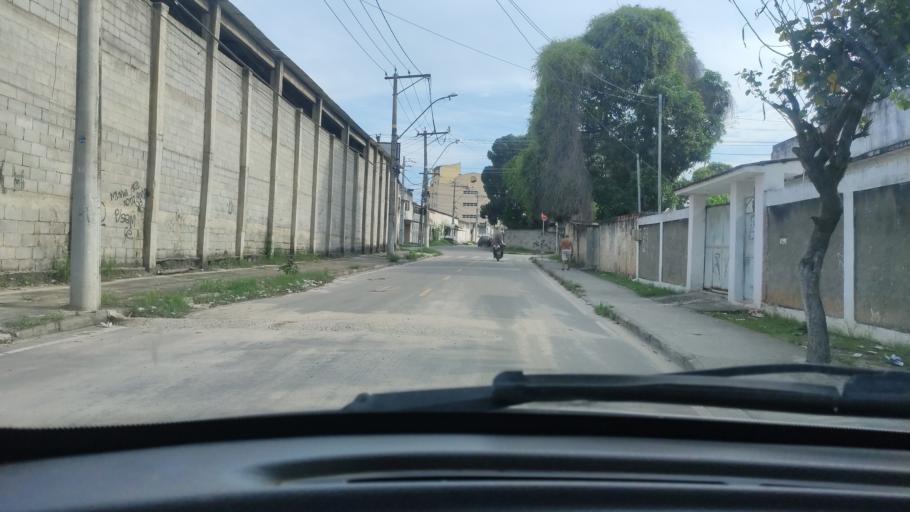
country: BR
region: Rio de Janeiro
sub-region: Itaborai
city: Itaborai
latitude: -22.7780
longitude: -42.9379
